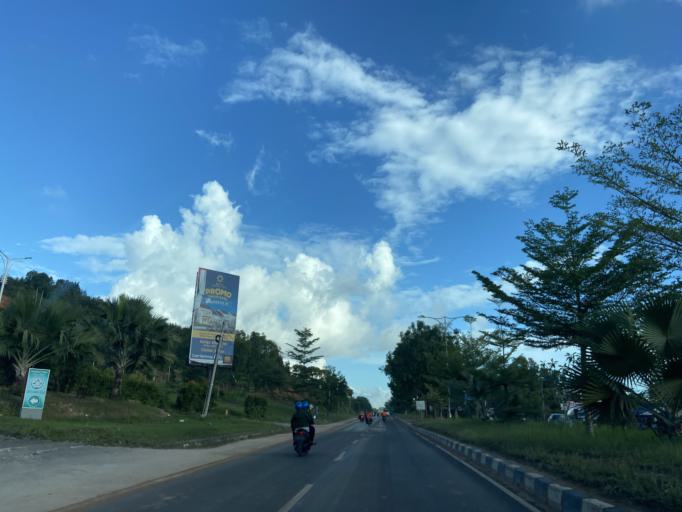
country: SG
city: Singapore
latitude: 1.0289
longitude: 104.0054
